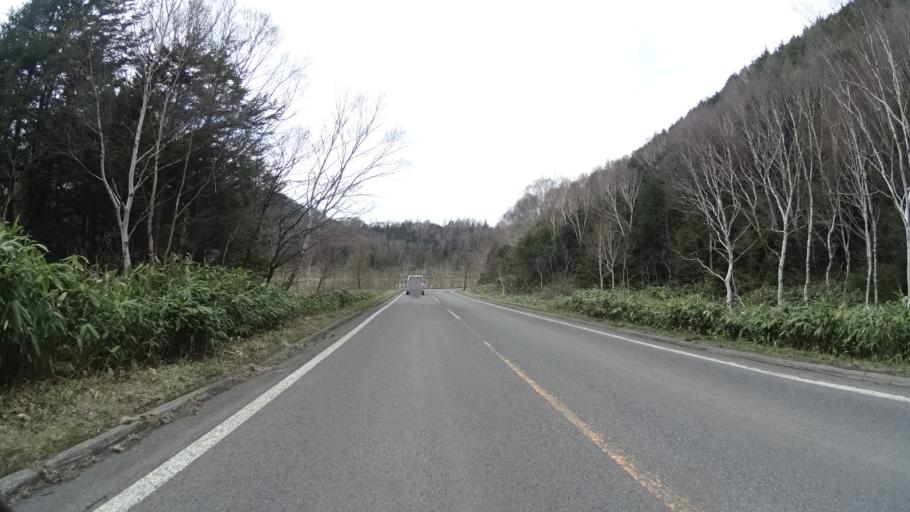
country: JP
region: Nagano
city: Nakano
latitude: 36.7006
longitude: 138.4926
